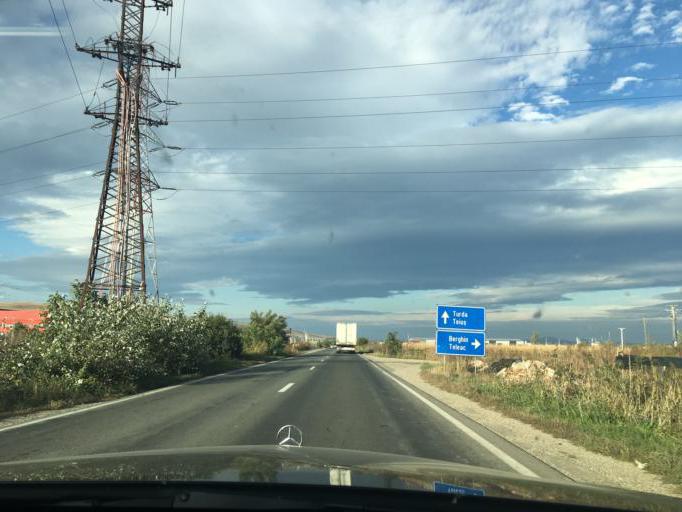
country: RO
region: Alba
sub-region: Municipiul Alba Iulia
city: Barabant
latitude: 46.0903
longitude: 23.5997
